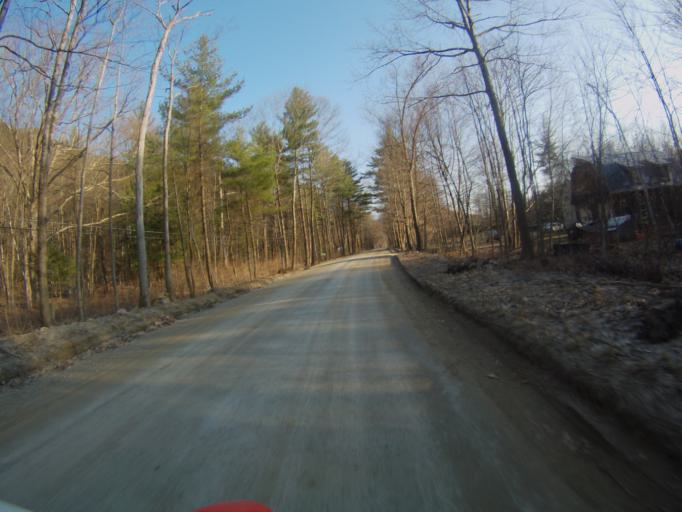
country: US
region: Vermont
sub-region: Addison County
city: Bristol
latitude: 44.1083
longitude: -73.0762
